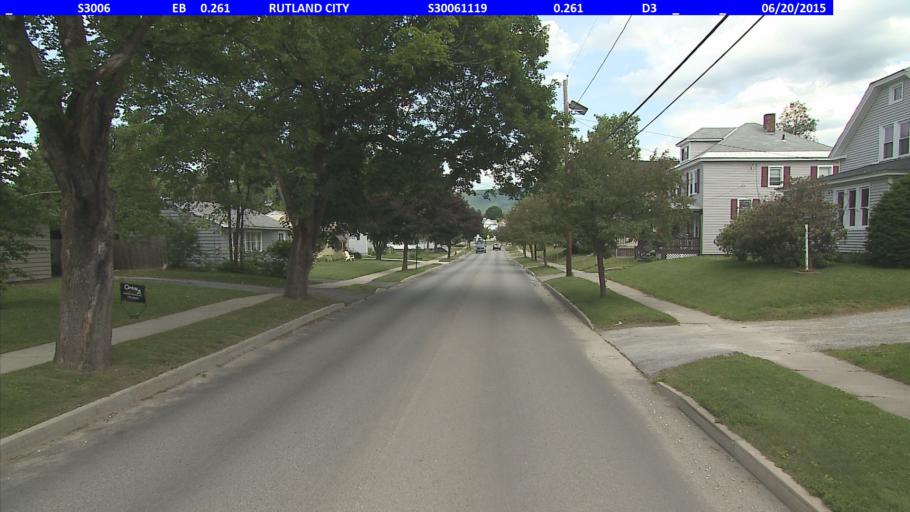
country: US
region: Vermont
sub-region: Rutland County
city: Rutland
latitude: 43.6147
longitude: -72.9867
